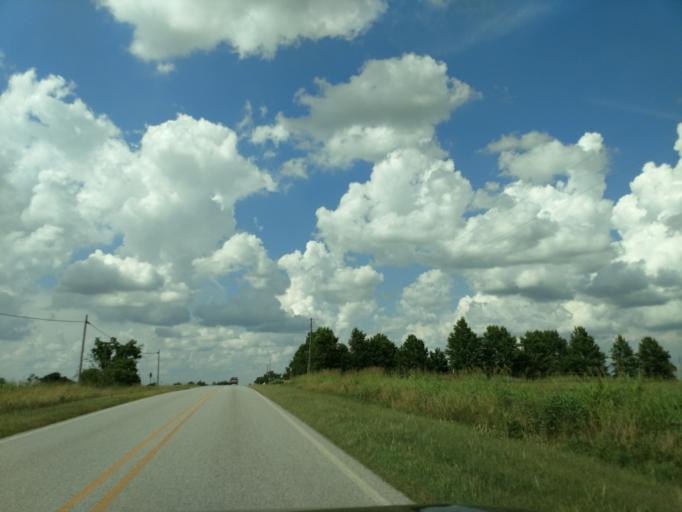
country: US
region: Arkansas
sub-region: Carroll County
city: Berryville
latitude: 36.4356
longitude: -93.5563
